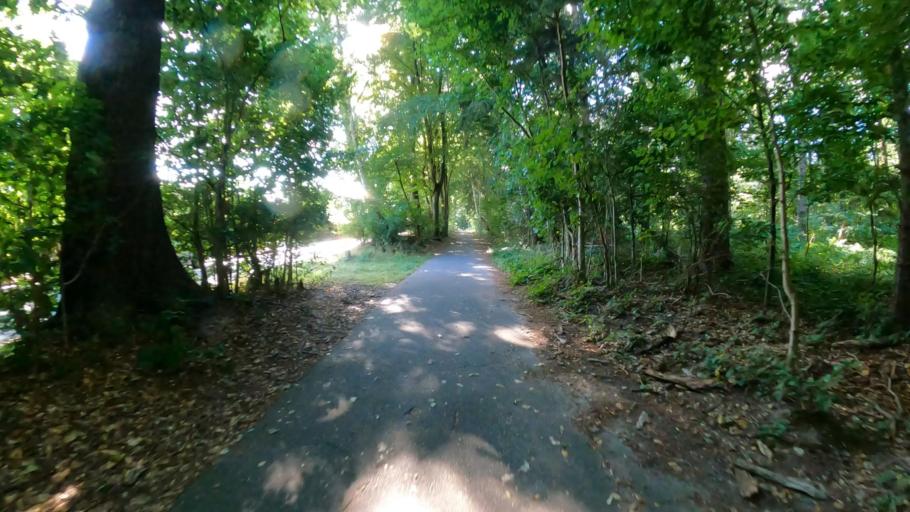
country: DE
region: Schleswig-Holstein
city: Ahrensburg
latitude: 53.6458
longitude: 10.2225
